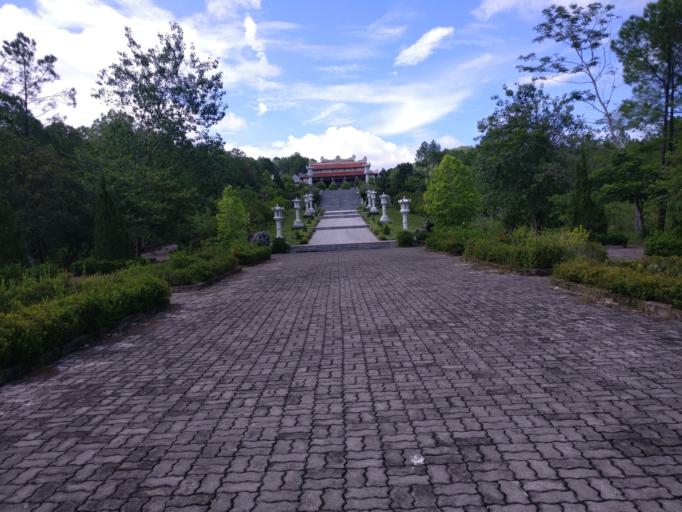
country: VN
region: Thua Thien-Hue
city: Hue
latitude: 16.4193
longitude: 107.6093
